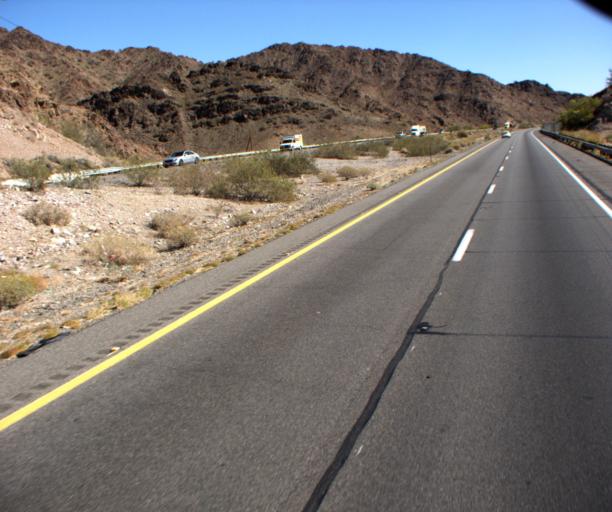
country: US
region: Arizona
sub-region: La Paz County
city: Quartzsite
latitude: 33.6456
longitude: -114.3779
